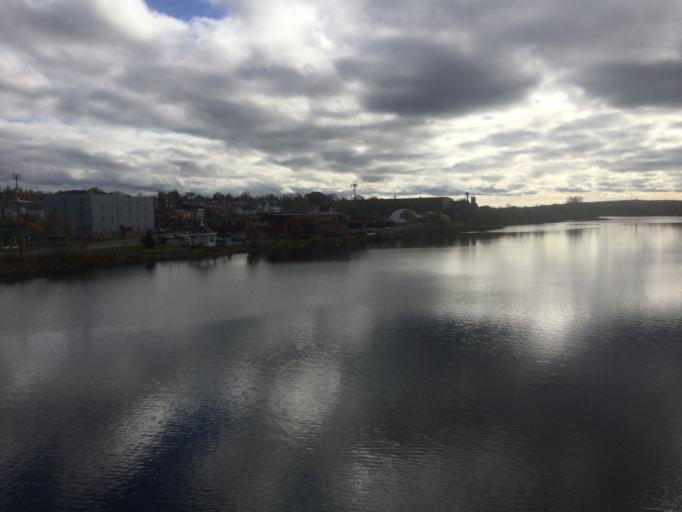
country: CA
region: Nova Scotia
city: New Glasgow
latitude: 45.5896
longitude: -62.6469
